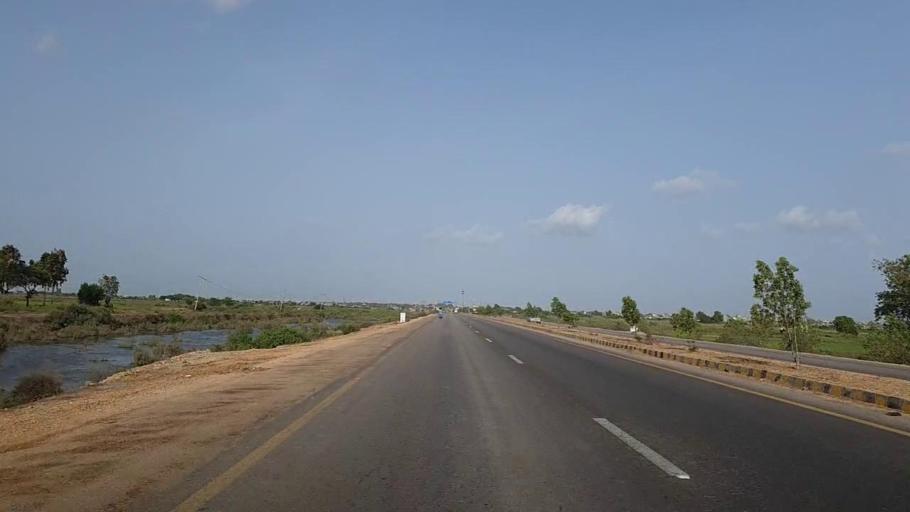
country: PK
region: Sindh
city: Thatta
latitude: 24.7453
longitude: 67.8641
